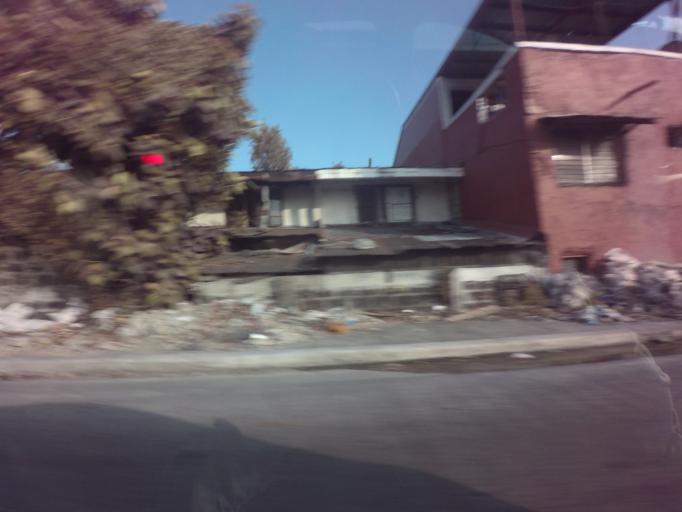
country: PH
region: Metro Manila
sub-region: Makati City
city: Makati City
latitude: 14.5089
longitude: 121.0292
